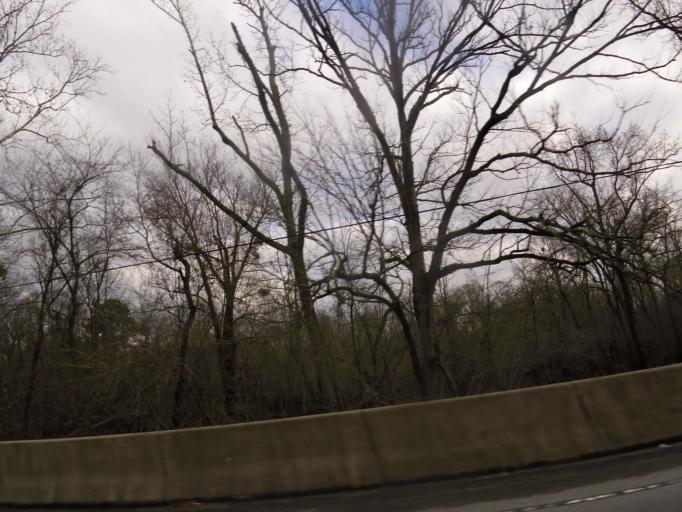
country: US
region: North Carolina
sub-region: Edgecombe County
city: Pinetops
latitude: 35.8211
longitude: -77.6590
